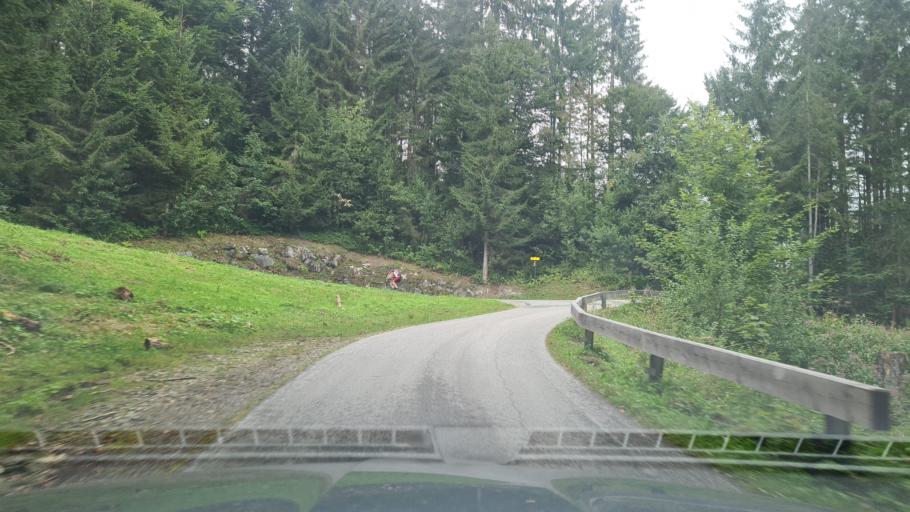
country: AT
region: Salzburg
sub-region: Politischer Bezirk Sankt Johann im Pongau
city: Sankt Johann im Pongau
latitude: 47.3592
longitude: 13.1823
